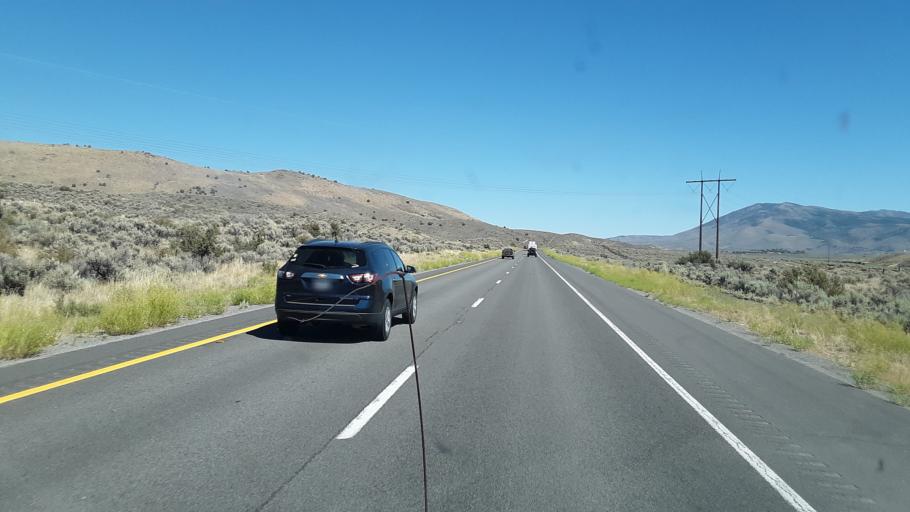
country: US
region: Nevada
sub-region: Washoe County
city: Cold Springs
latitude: 39.6965
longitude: -120.0264
